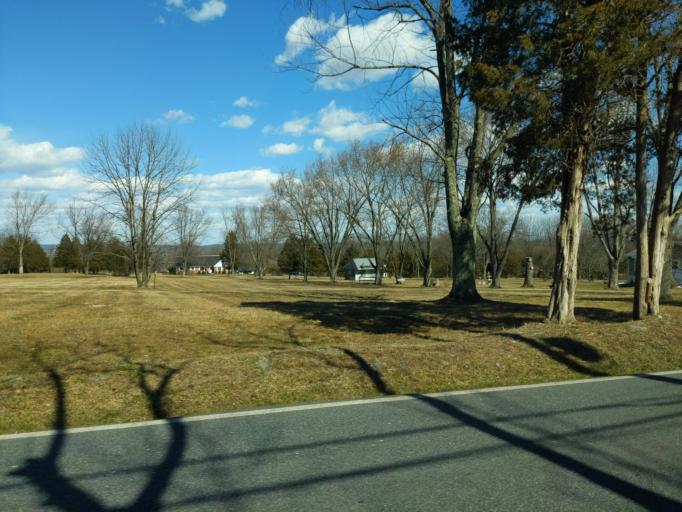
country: US
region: Pennsylvania
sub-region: Montgomery County
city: Red Hill
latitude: 40.3483
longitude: -75.5155
